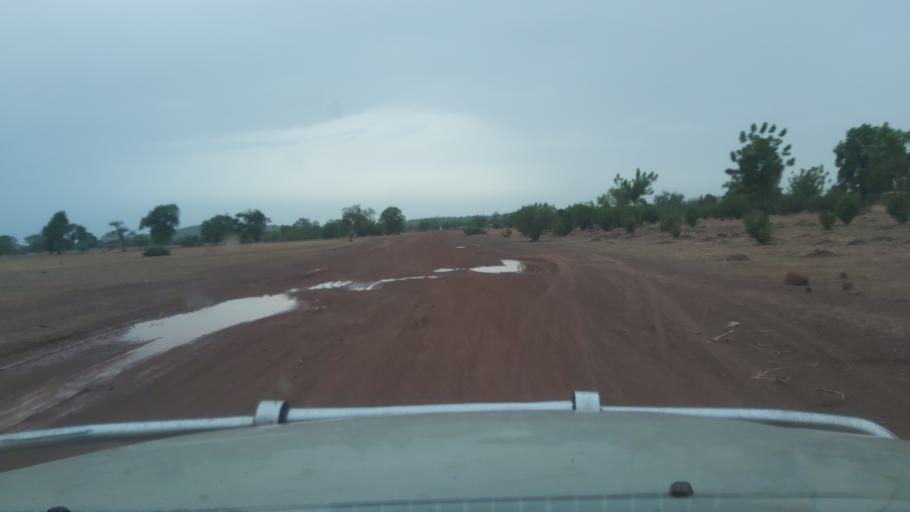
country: ML
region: Koulikoro
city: Banamba
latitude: 13.2819
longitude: -7.5557
